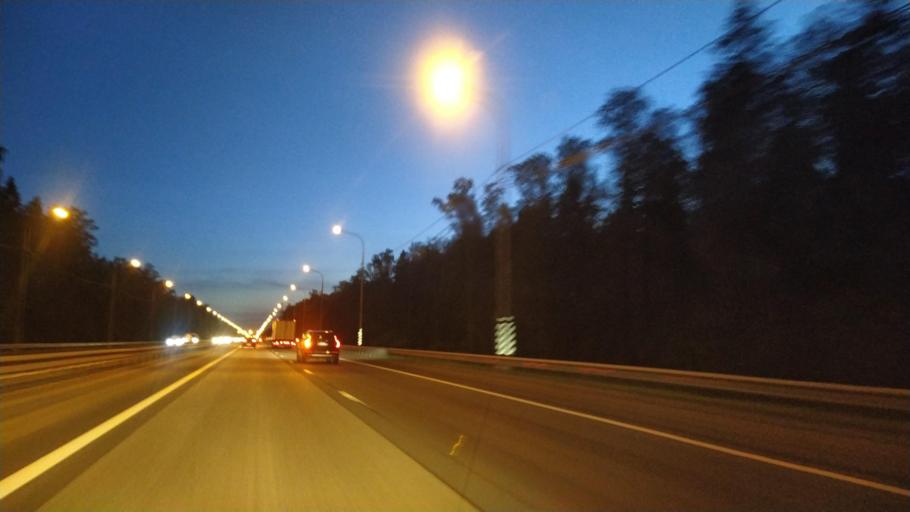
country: RU
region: Leningrad
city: Yanino Vtoroye
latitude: 59.8896
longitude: 30.5772
